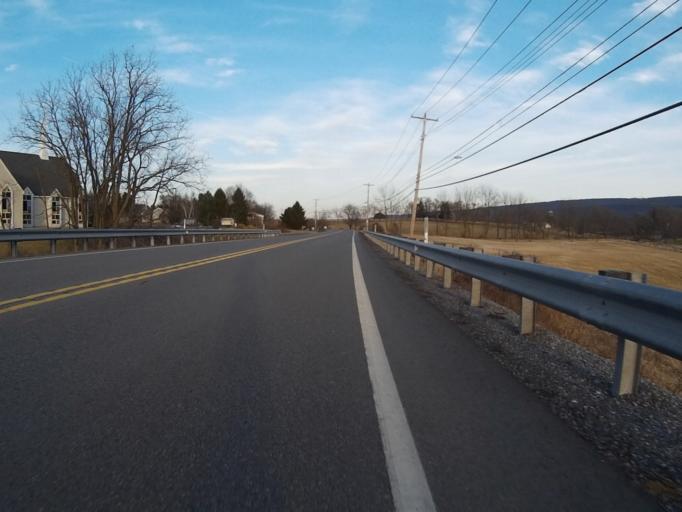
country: US
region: Pennsylvania
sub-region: Centre County
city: Pine Grove Mills
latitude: 40.7289
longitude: -77.9341
